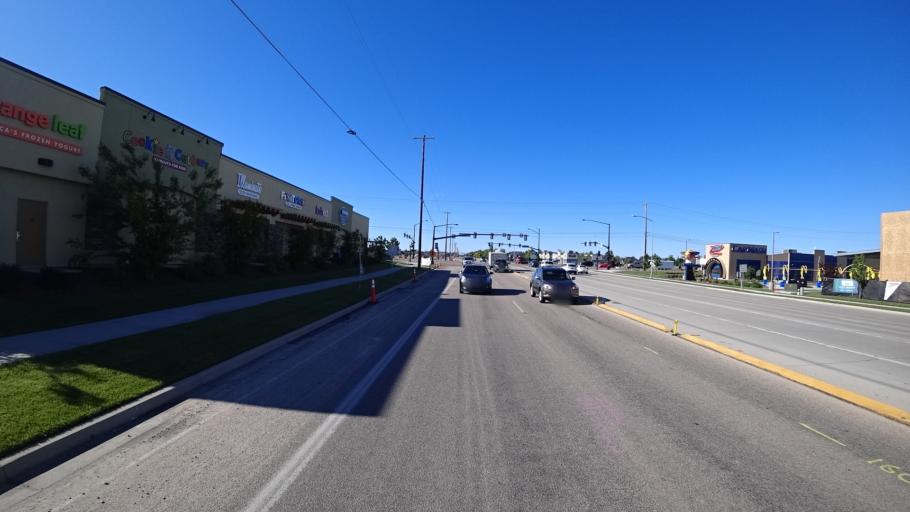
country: US
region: Idaho
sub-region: Ada County
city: Meridian
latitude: 43.6639
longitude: -116.4136
